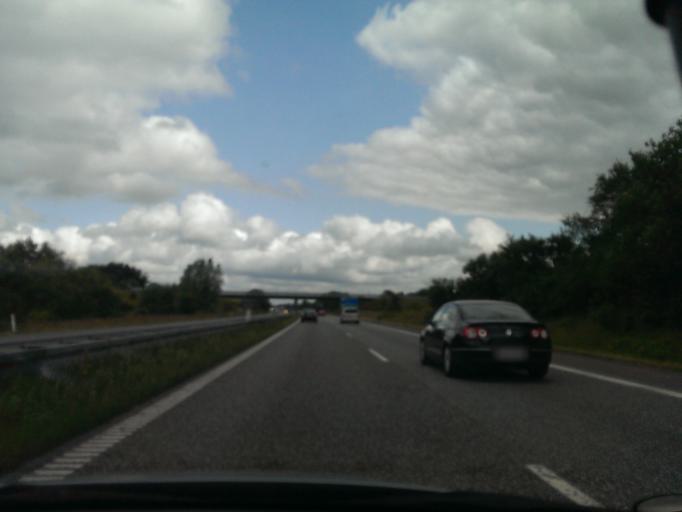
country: DK
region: North Denmark
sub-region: Mariagerfjord Kommune
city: Hobro
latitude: 56.6515
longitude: 9.7379
